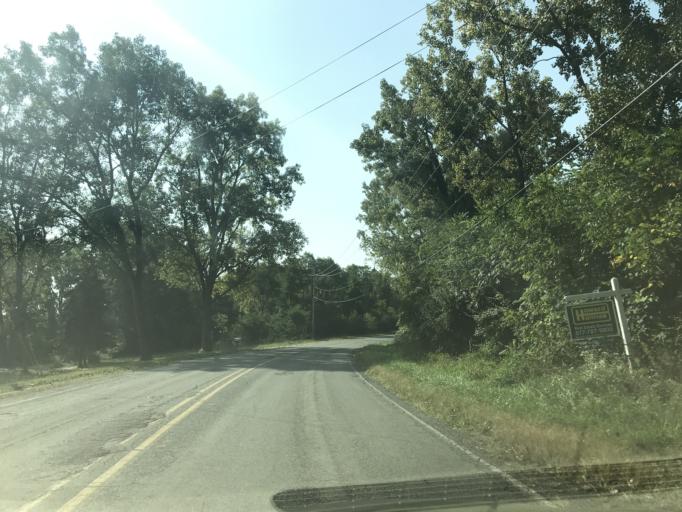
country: US
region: Michigan
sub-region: Jackson County
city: Jackson
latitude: 42.2936
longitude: -84.4340
